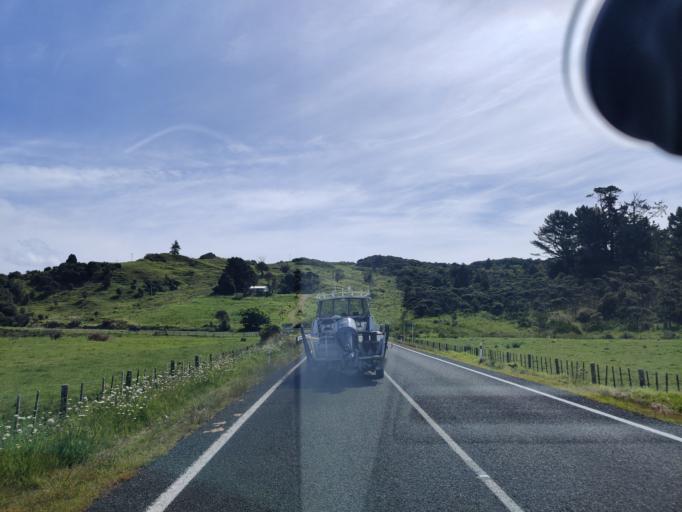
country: NZ
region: Northland
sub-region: Far North District
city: Kaitaia
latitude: -35.4746
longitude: 173.4604
